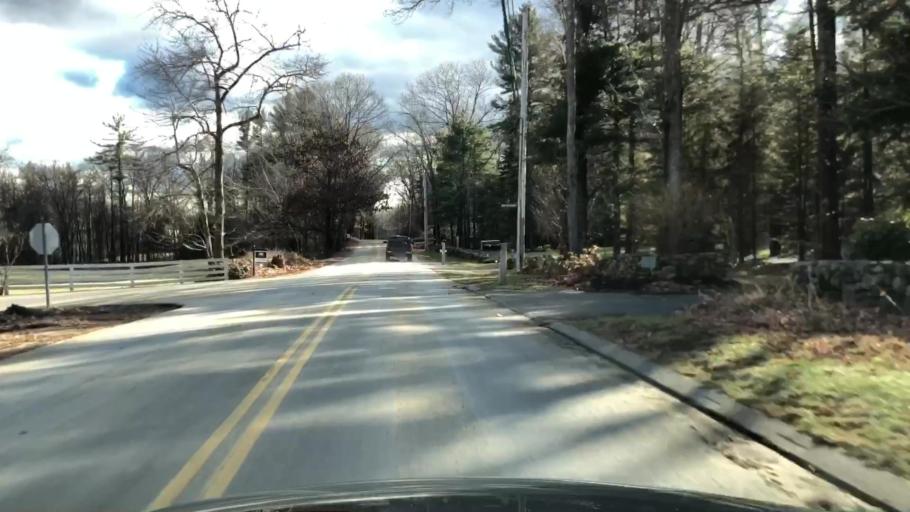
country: US
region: New Hampshire
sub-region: Hillsborough County
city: Mont Vernon
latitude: 42.8876
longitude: -71.6325
